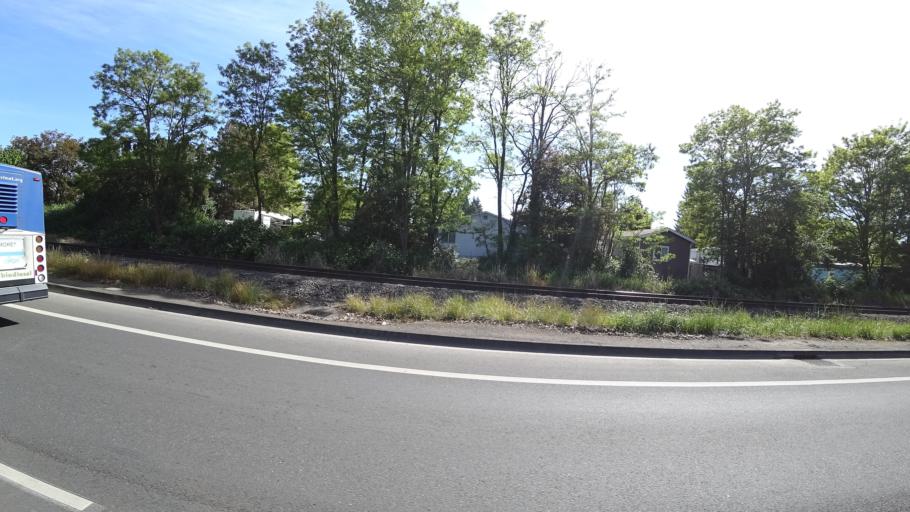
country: US
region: Oregon
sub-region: Washington County
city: Hillsboro
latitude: 45.5073
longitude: -122.9626
